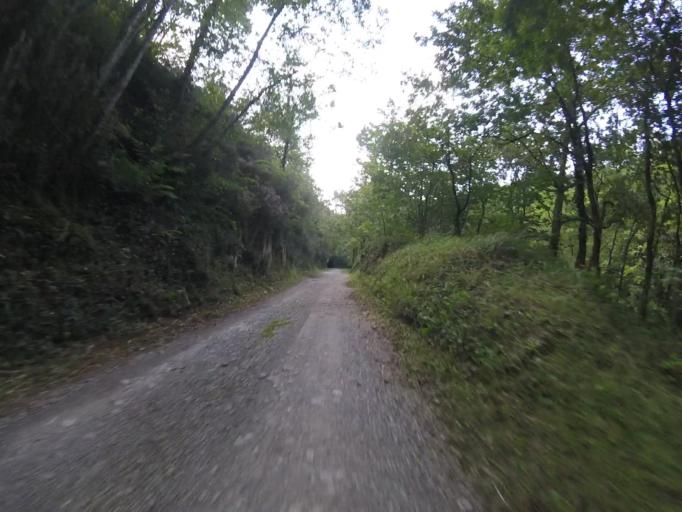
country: ES
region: Basque Country
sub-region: Provincia de Guipuzcoa
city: Elduayen
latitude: 43.1743
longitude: -1.9700
